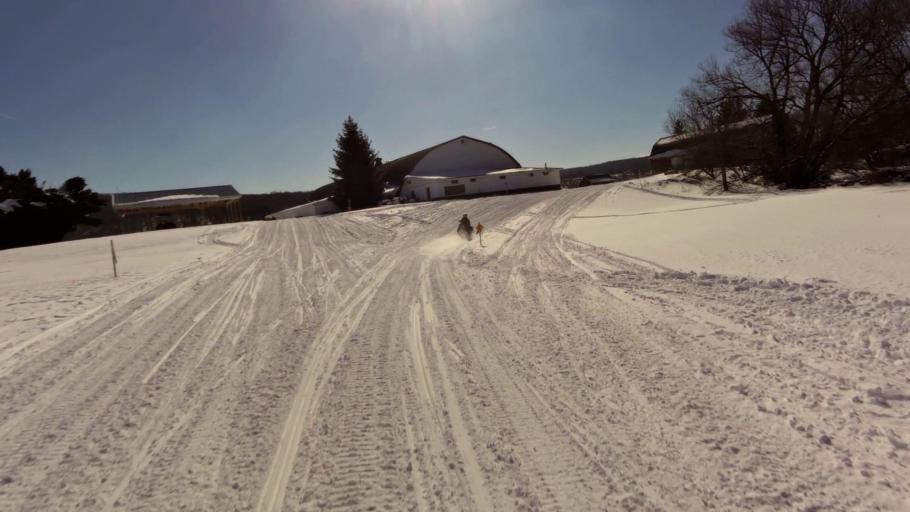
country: US
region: New York
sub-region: Cattaraugus County
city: Franklinville
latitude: 42.3555
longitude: -78.4535
